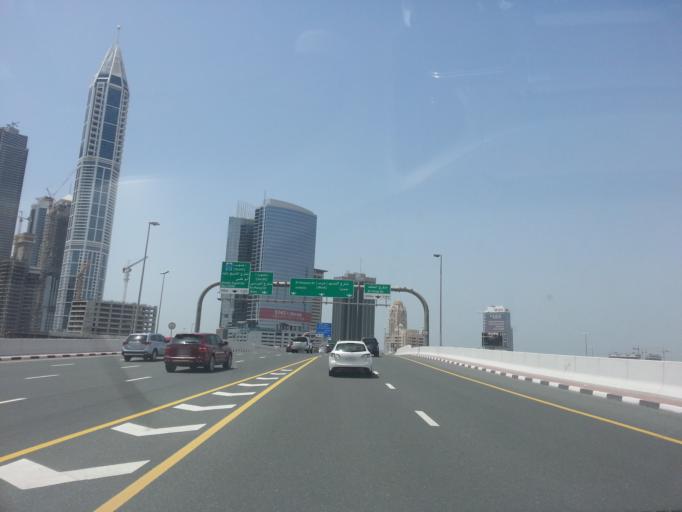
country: AE
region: Dubai
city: Dubai
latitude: 25.0847
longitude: 55.1544
